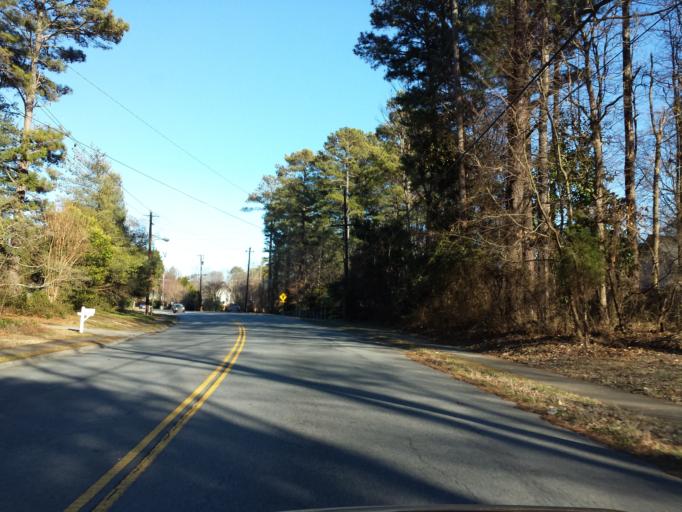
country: US
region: Georgia
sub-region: Cobb County
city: Smyrna
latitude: 33.9416
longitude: -84.4698
